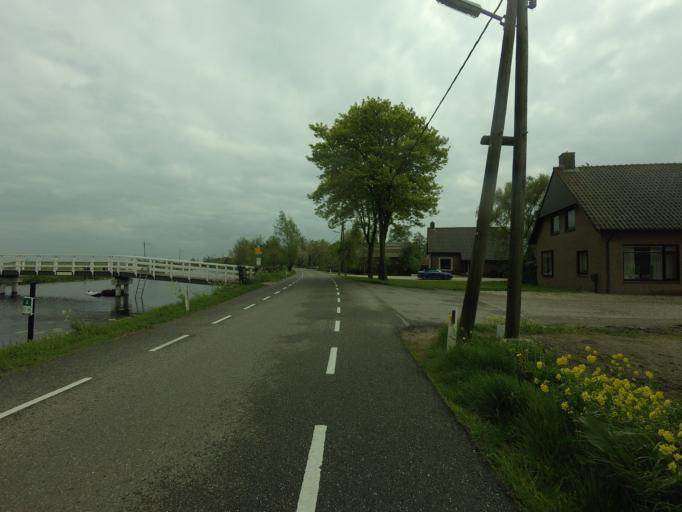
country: NL
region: South Holland
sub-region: Gemeente Vlist
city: Vlist
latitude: 51.9884
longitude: 4.8060
